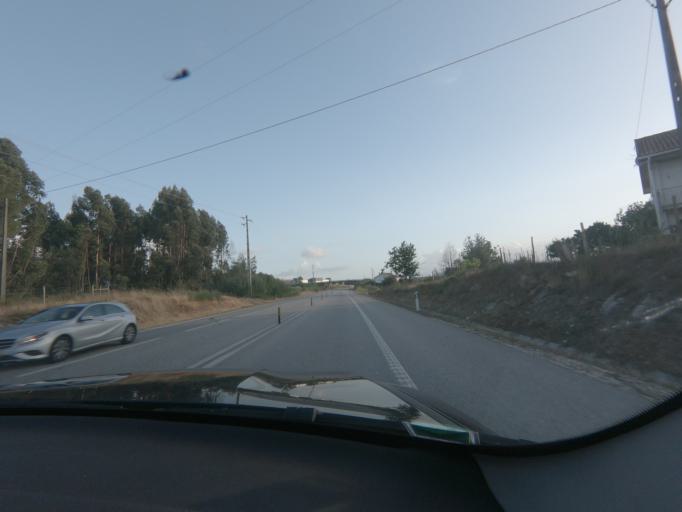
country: PT
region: Viseu
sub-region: Santa Comba Dao
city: Santa Comba Dao
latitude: 40.3637
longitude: -8.1334
